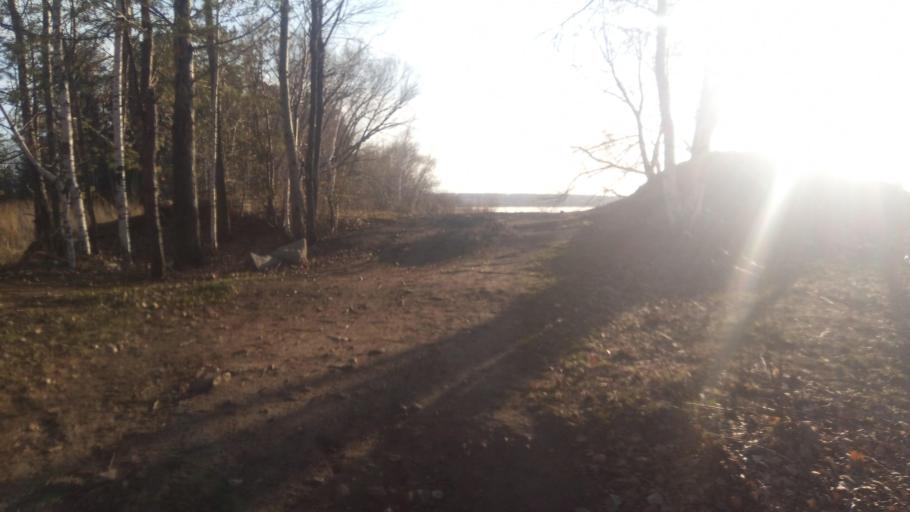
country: RU
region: Chelyabinsk
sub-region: Gorod Chelyabinsk
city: Chelyabinsk
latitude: 55.1396
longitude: 61.3299
